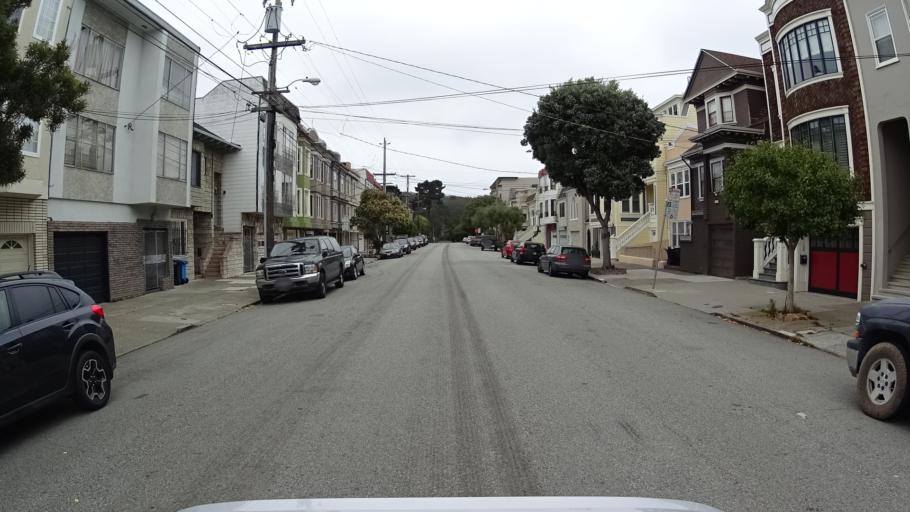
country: US
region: California
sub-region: San Francisco County
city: San Francisco
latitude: 37.7851
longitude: -122.4710
